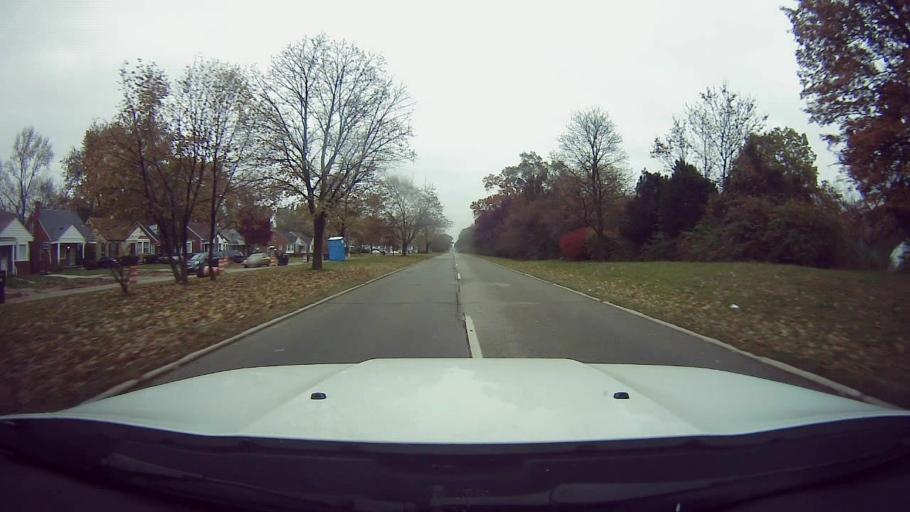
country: US
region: Michigan
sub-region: Wayne County
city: Dearborn Heights
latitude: 42.3660
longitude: -83.2606
